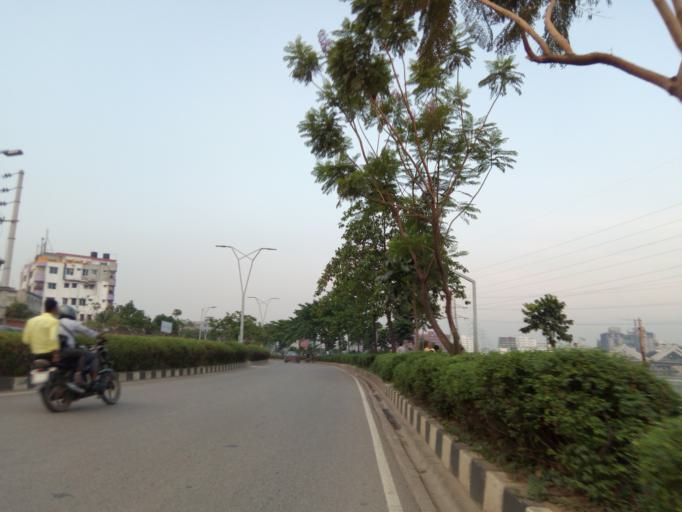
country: BD
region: Dhaka
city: Paltan
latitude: 23.7708
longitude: 90.4197
